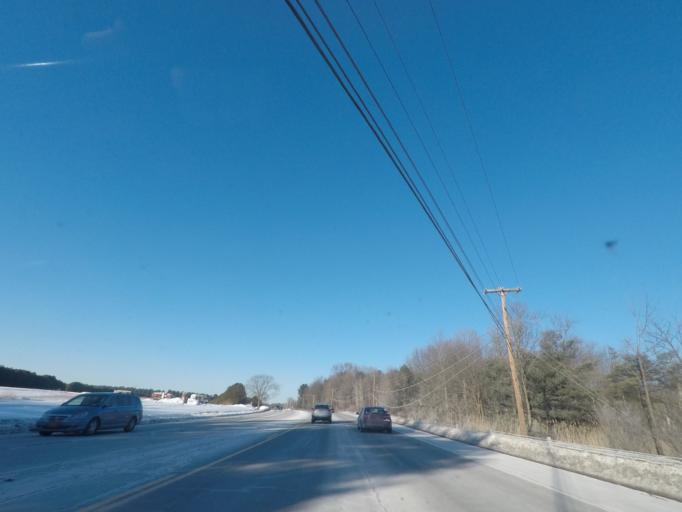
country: US
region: New York
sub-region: Saratoga County
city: Saratoga Springs
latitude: 43.0493
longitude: -73.7885
